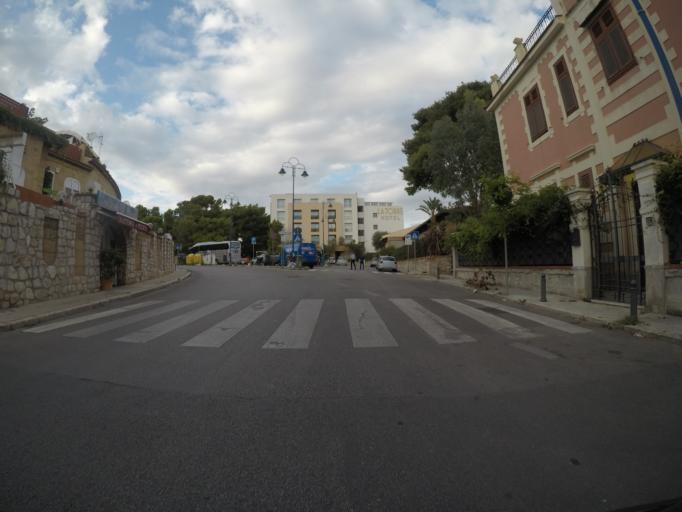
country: IT
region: Sicily
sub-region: Palermo
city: Palermo
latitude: 38.2097
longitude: 13.3291
